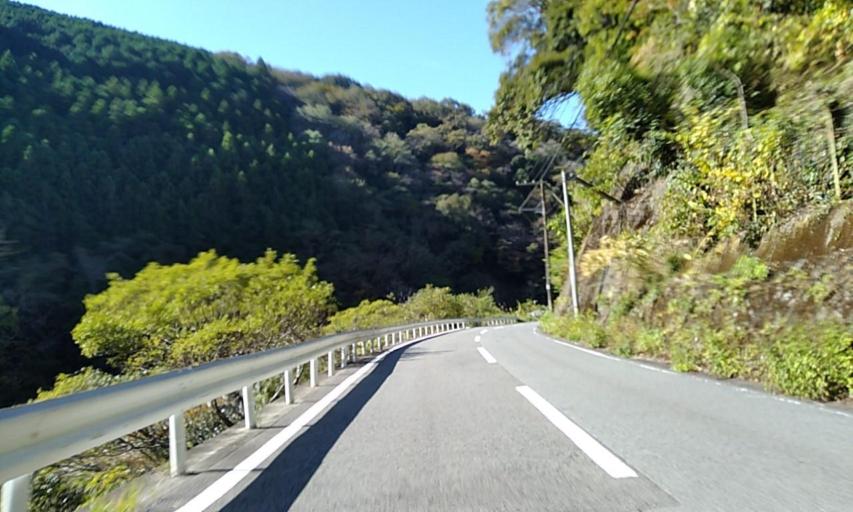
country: JP
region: Wakayama
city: Kainan
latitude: 34.0612
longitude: 135.3577
